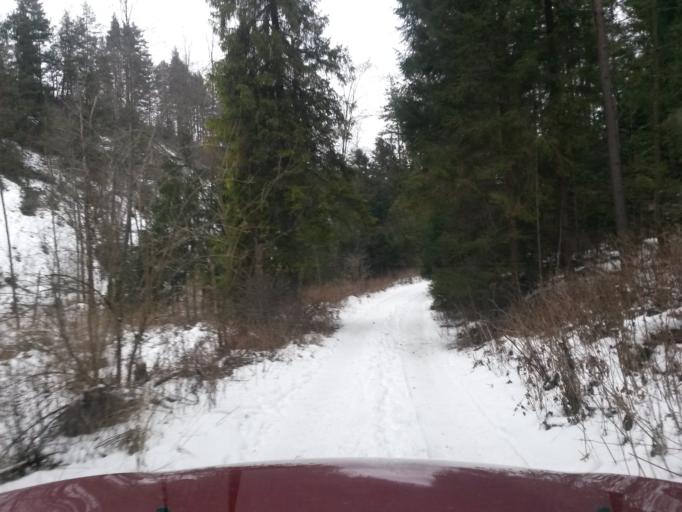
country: SK
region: Kosicky
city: Spisska Nova Ves
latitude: 48.8749
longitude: 20.5826
